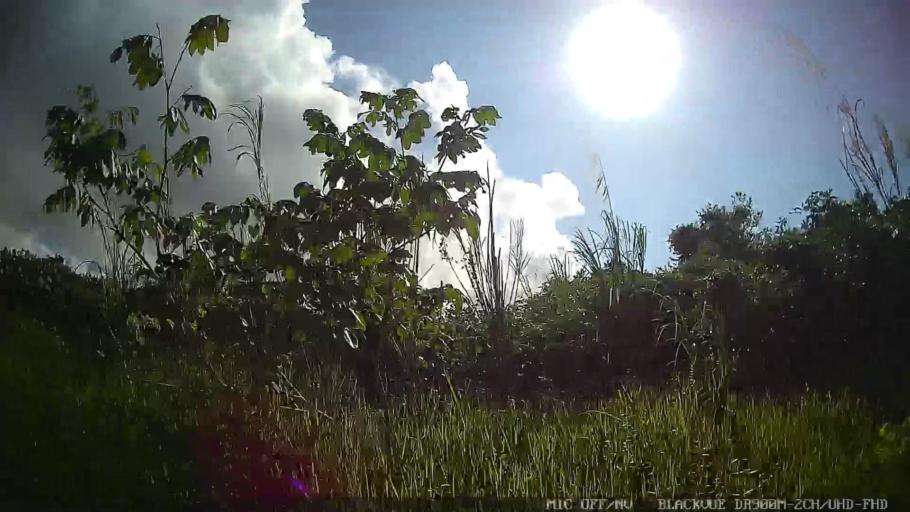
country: BR
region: Sao Paulo
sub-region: Peruibe
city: Peruibe
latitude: -24.2674
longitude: -46.9306
